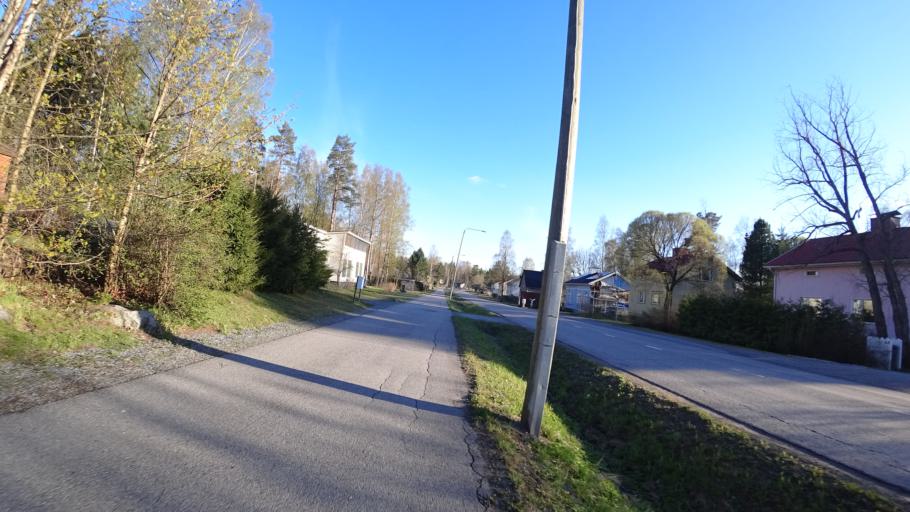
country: FI
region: Pirkanmaa
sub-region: Tampere
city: Yloejaervi
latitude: 61.5083
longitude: 23.5938
